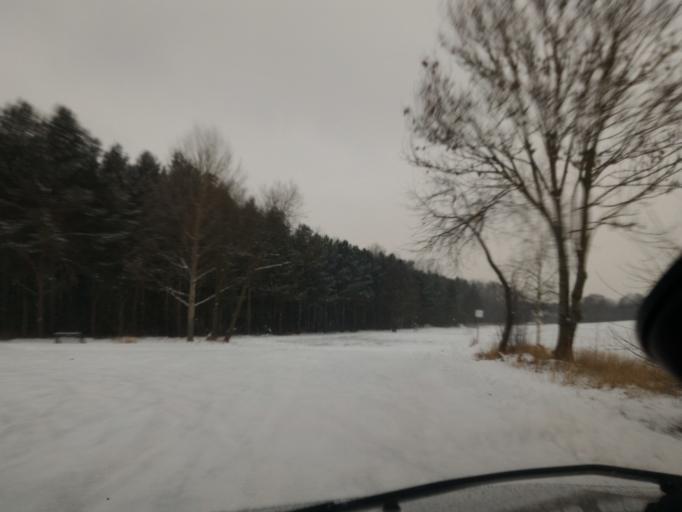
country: DE
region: Saxony
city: Grossschonau
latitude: 50.8819
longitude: 14.6683
